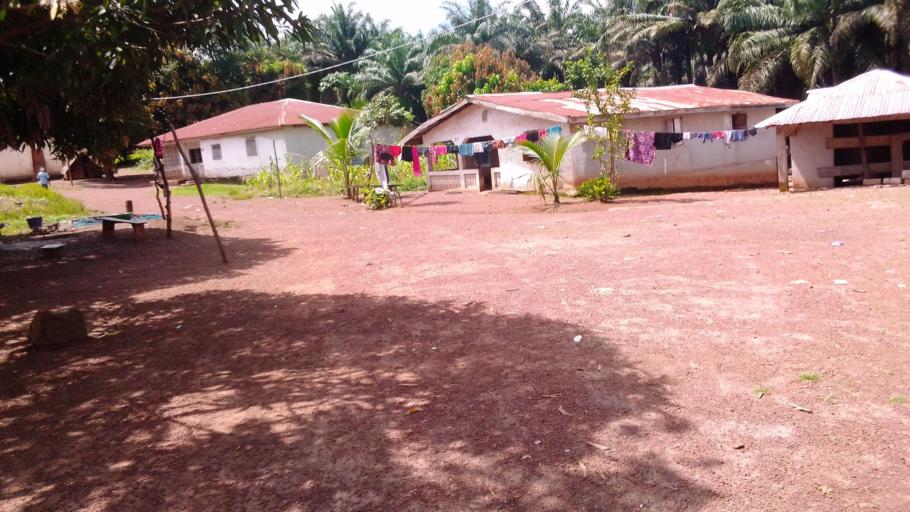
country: SL
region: Northern Province
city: Makeni
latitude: 8.8829
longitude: -12.0293
